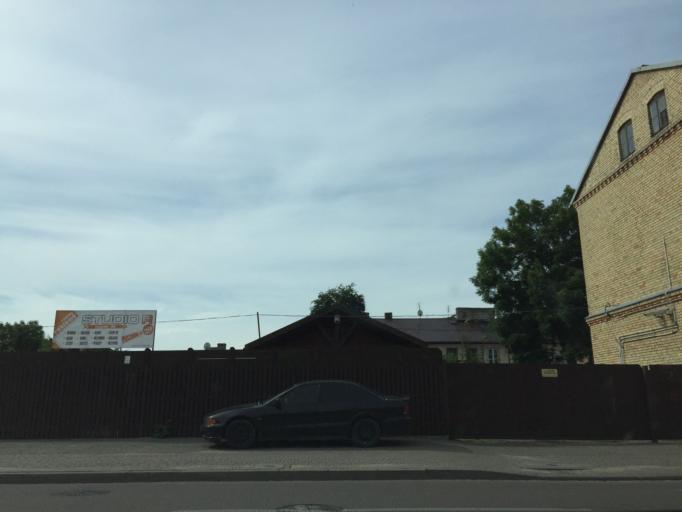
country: PL
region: Podlasie
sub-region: Suwalki
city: Suwalki
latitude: 54.0990
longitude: 22.9296
